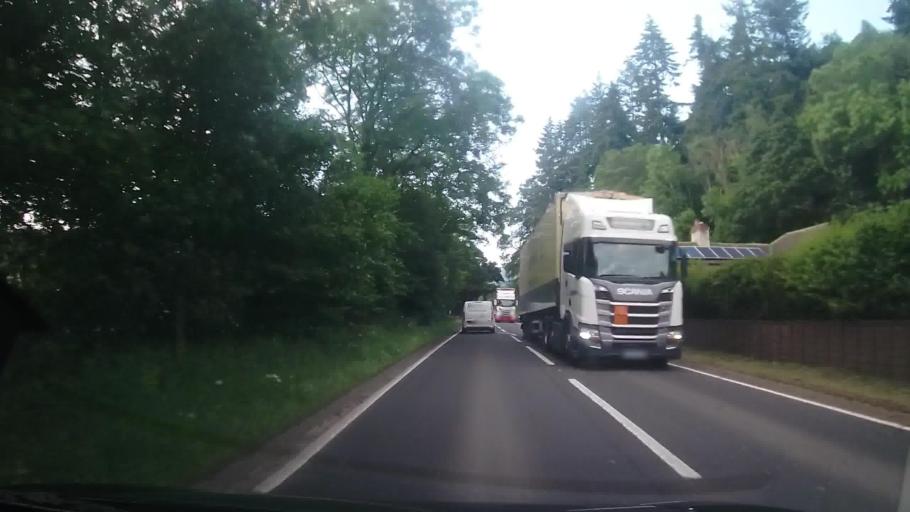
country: GB
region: England
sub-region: Shropshire
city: Church Stretton
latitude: 52.5061
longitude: -2.8245
